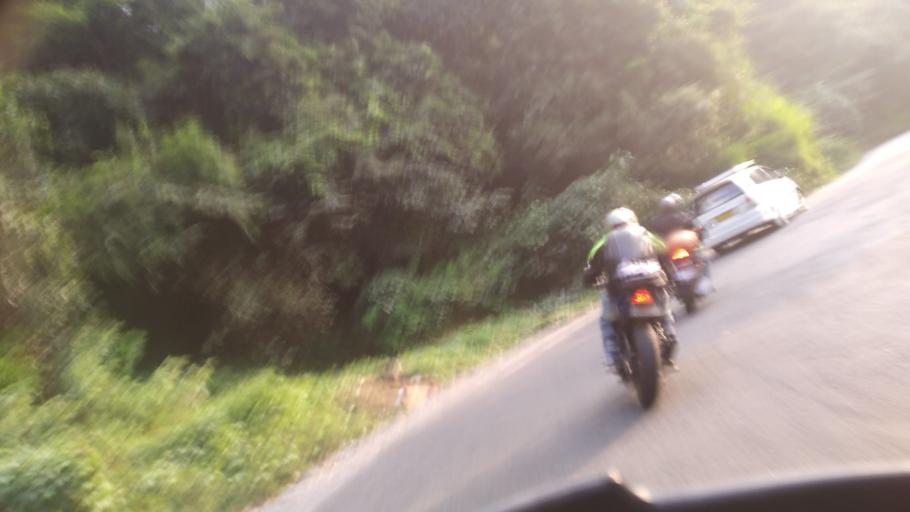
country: IN
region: Kerala
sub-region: Wayanad
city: Kalpetta
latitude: 11.5058
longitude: 76.0308
